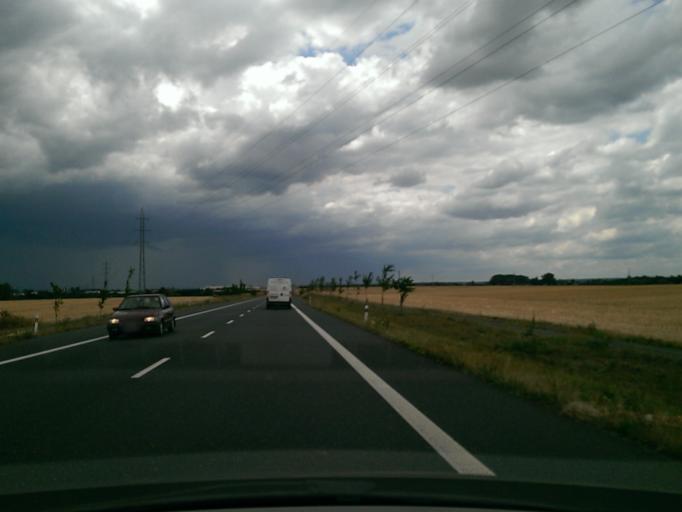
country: CZ
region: Central Bohemia
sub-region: Okres Nymburk
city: Nymburk
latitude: 50.1934
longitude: 15.0690
